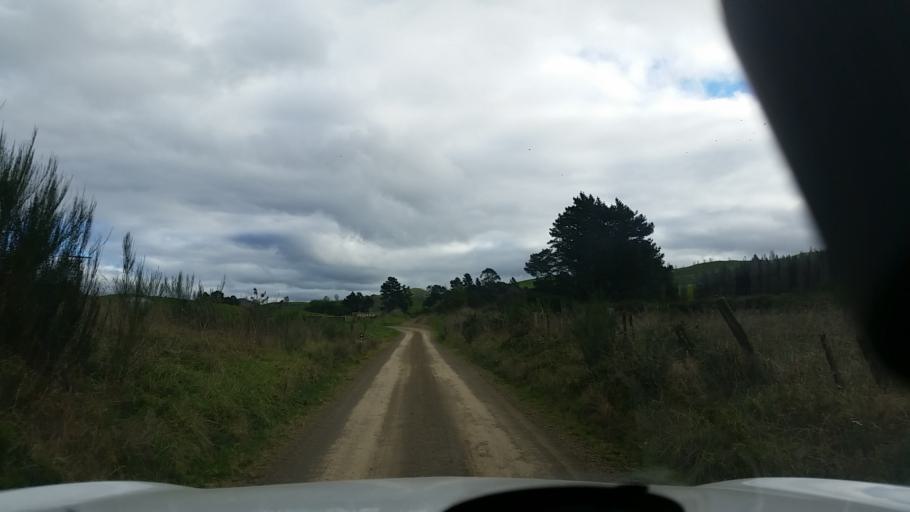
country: NZ
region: Hawke's Bay
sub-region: Napier City
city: Napier
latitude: -39.1987
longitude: 176.8757
